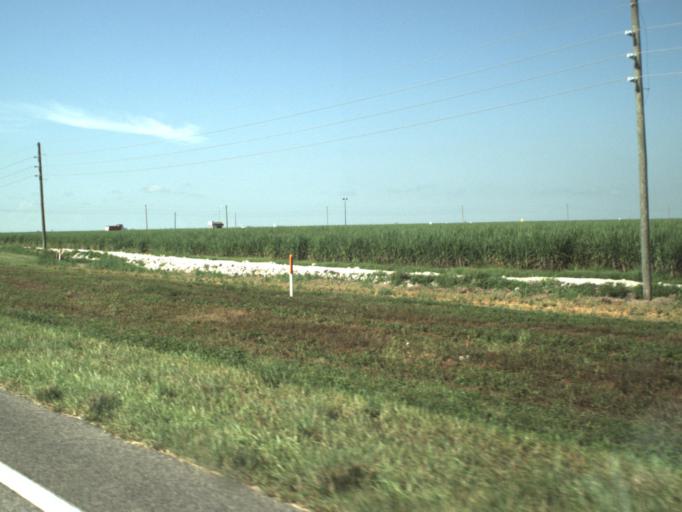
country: US
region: Florida
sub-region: Palm Beach County
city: Belle Glade Camp
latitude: 26.5838
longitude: -80.7111
